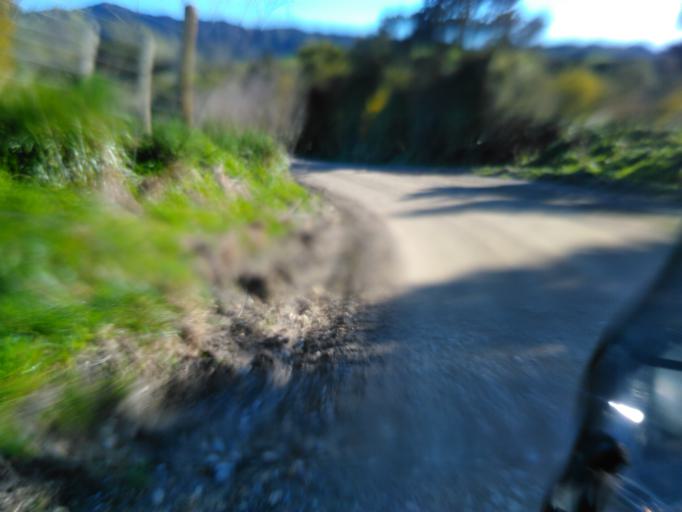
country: NZ
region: Gisborne
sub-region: Gisborne District
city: Gisborne
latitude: -38.3949
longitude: 177.6678
